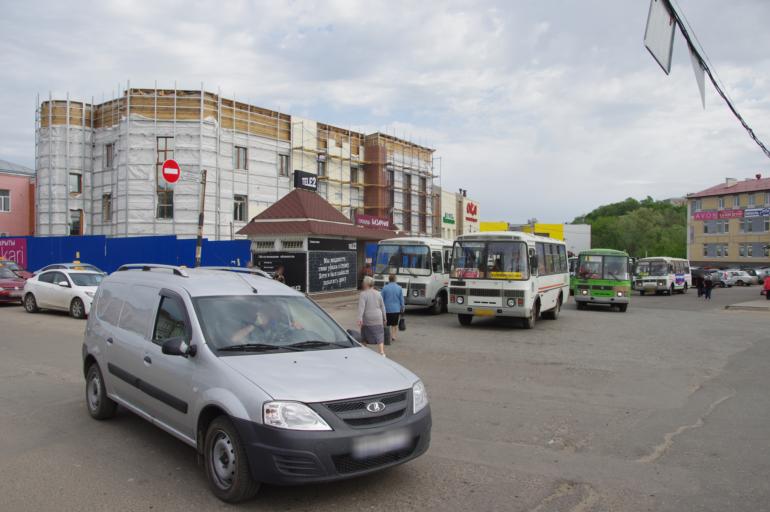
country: RU
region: Nizjnij Novgorod
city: Pavlovo
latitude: 55.9664
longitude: 43.0672
